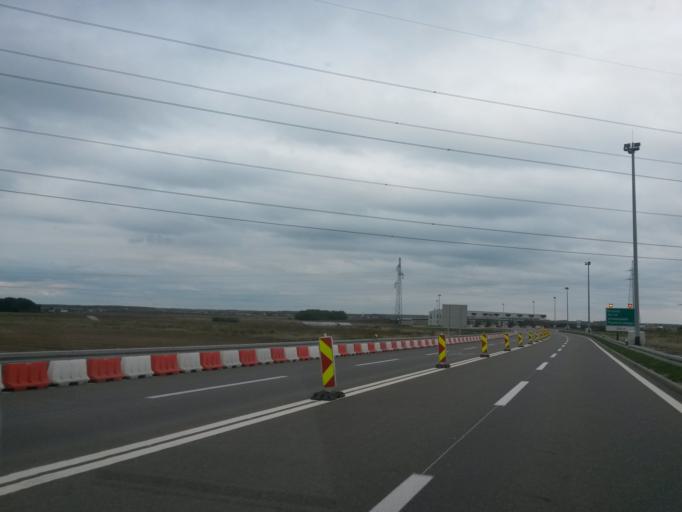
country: HR
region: Osjecko-Baranjska
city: Josipovac
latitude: 45.5750
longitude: 18.5546
